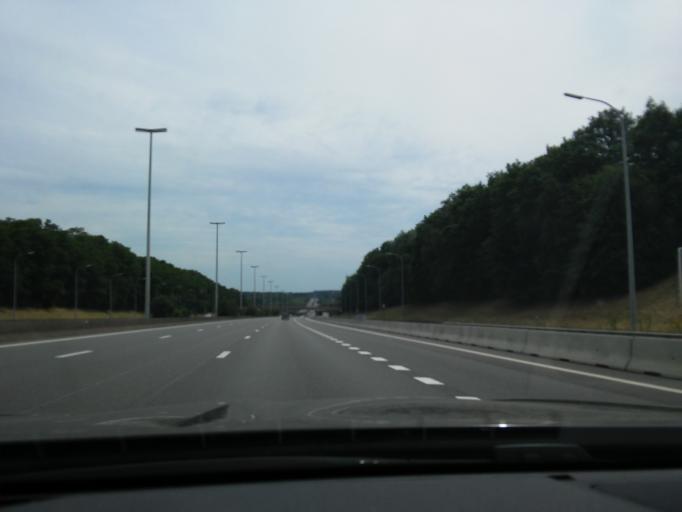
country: BE
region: Flanders
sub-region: Provincie Vlaams-Brabant
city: Bertem
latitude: 50.8561
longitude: 4.6458
